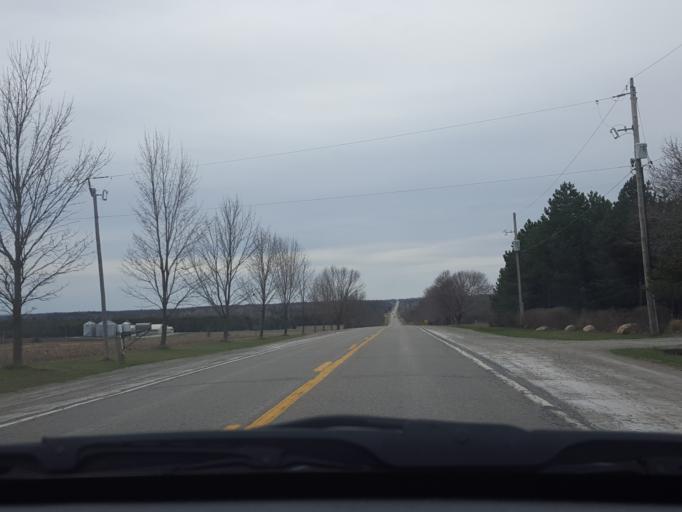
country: CA
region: Ontario
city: Uxbridge
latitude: 44.2788
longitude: -79.1629
